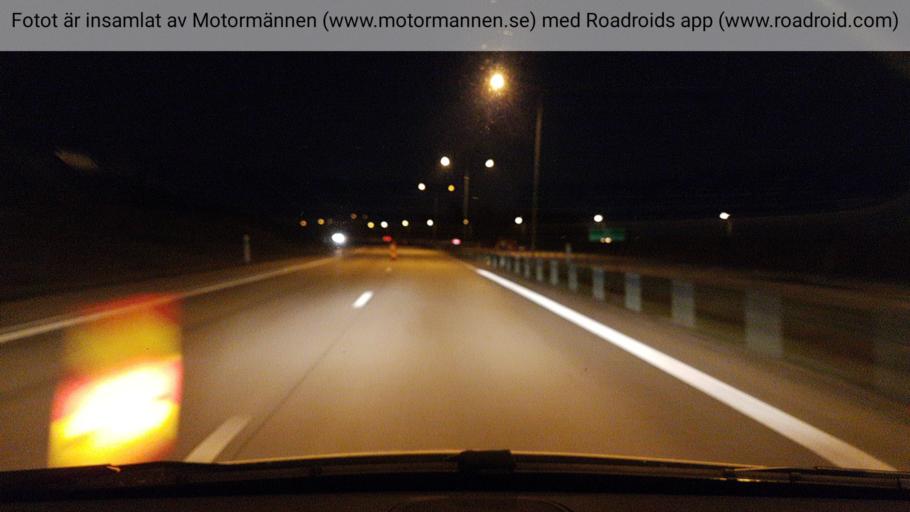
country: SE
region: Uppsala
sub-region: Uppsala Kommun
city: Saevja
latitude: 59.8333
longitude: 17.7396
